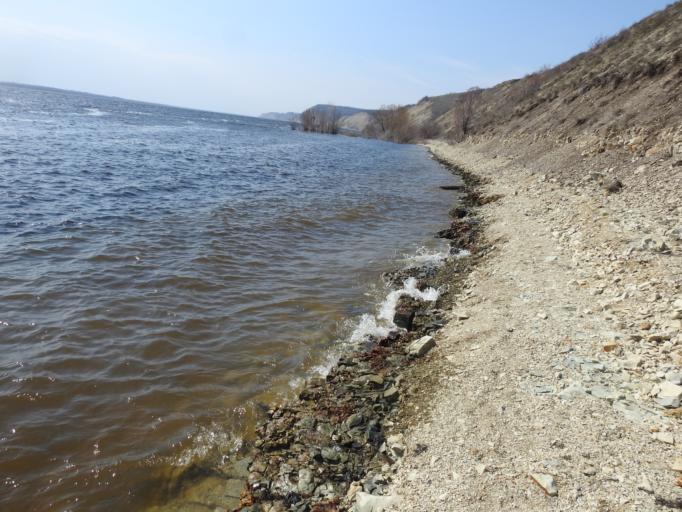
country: RU
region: Saratov
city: Voskresenskoye
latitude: 51.7946
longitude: 46.8671
